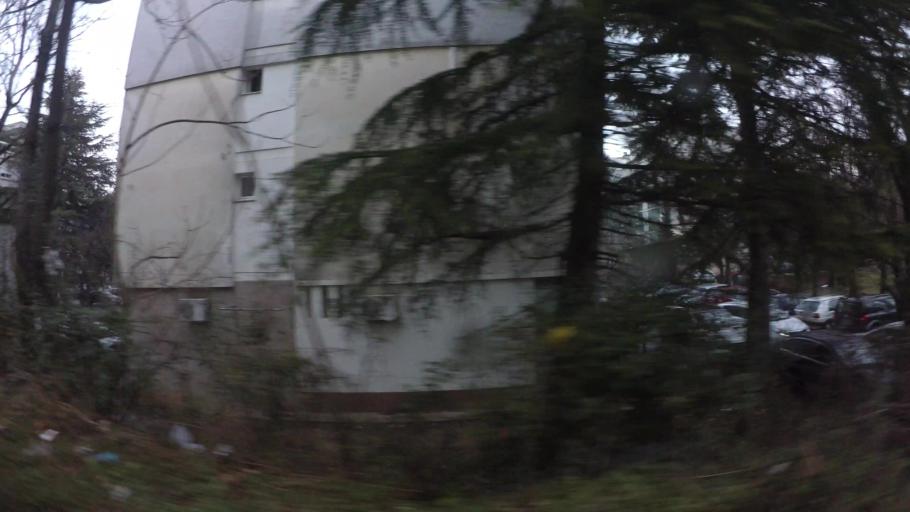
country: BA
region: Federation of Bosnia and Herzegovina
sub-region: Hercegovacko-Bosanski Kanton
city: Mostar
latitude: 43.3496
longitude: 17.7959
